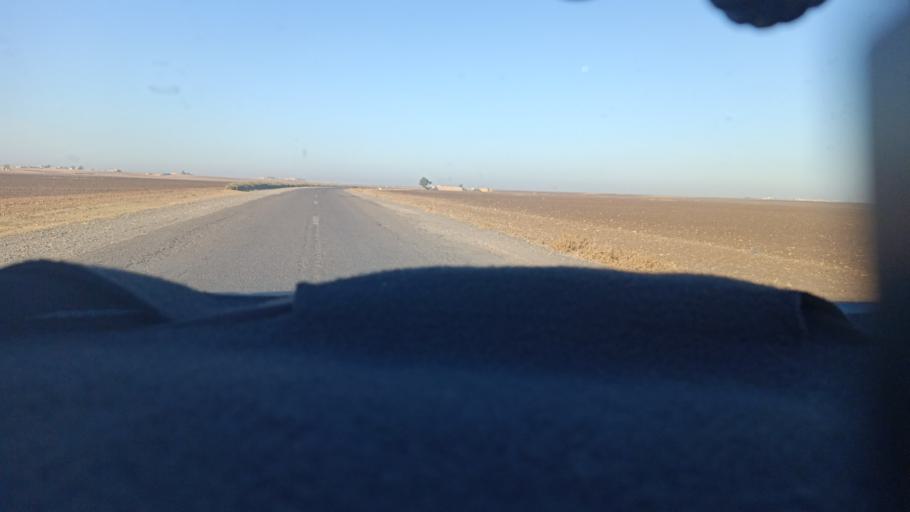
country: MA
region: Doukkala-Abda
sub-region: Safi
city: Youssoufia
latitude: 32.3717
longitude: -8.7084
